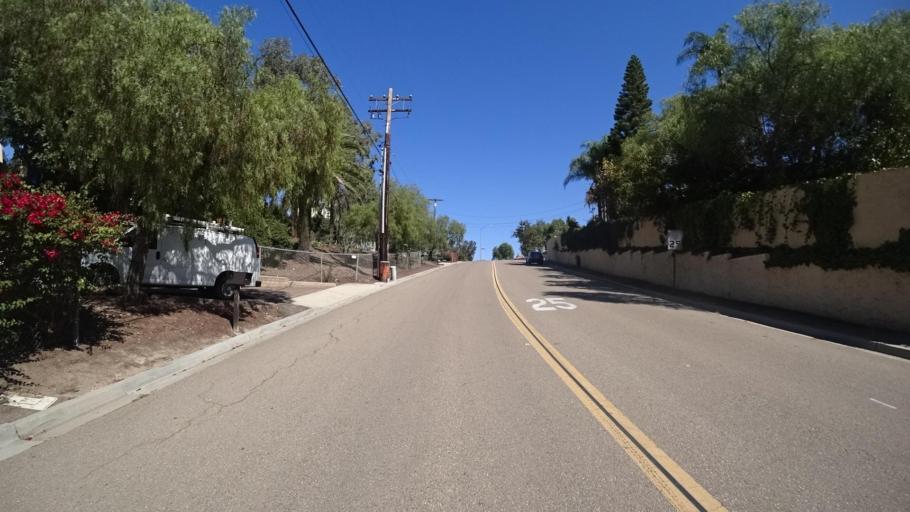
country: US
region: California
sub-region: San Diego County
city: Bonita
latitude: 32.6621
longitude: -117.0210
